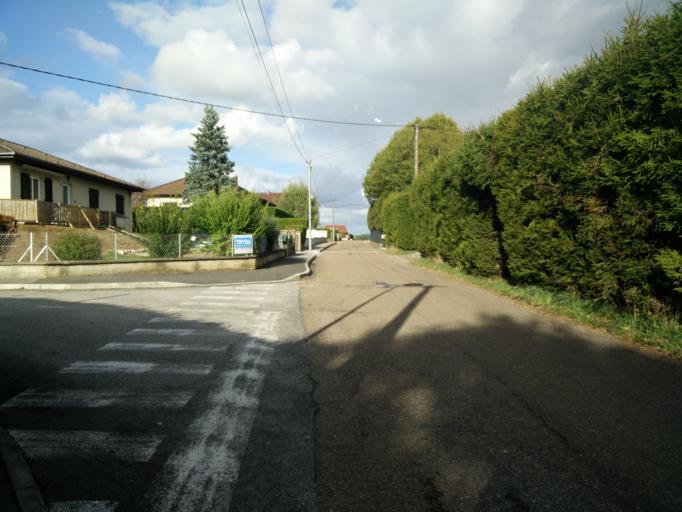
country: FR
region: Franche-Comte
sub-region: Departement du Doubs
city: Saone
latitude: 47.2273
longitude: 6.1248
